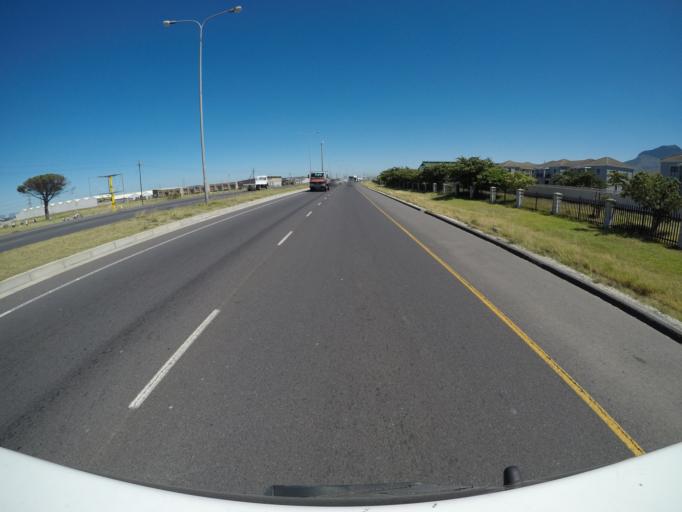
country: ZA
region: Western Cape
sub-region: Overberg District Municipality
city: Grabouw
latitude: -34.1063
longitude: 18.8580
